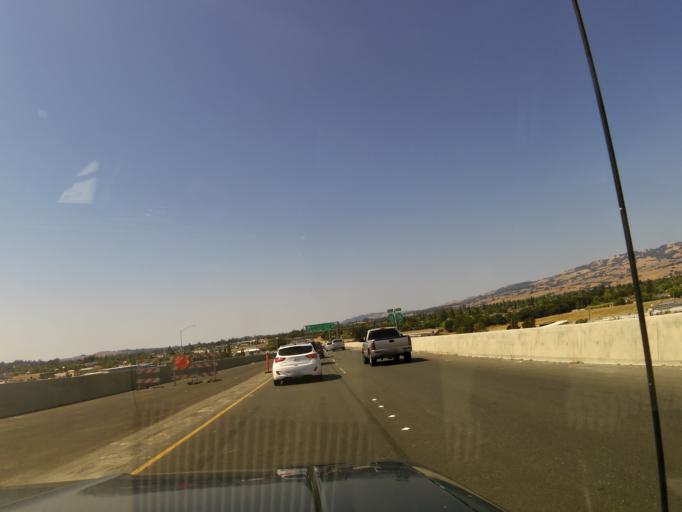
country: US
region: California
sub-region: Sonoma County
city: Petaluma
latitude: 38.2305
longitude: -122.6163
